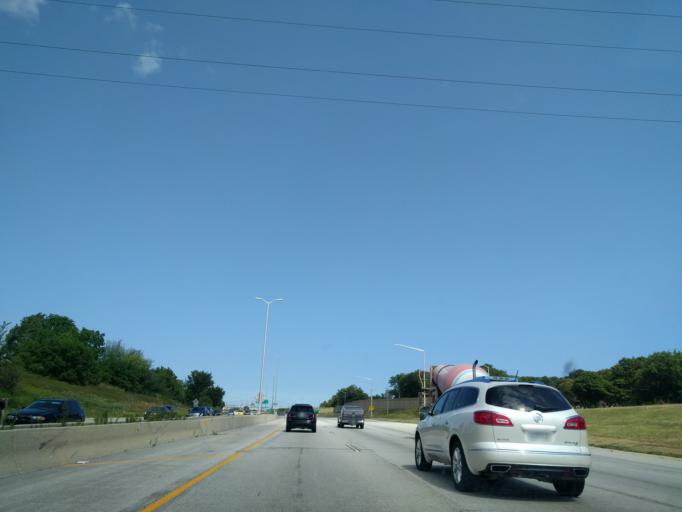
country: US
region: Wisconsin
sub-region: Milwaukee County
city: Saint Francis
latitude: 42.9741
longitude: -87.9156
